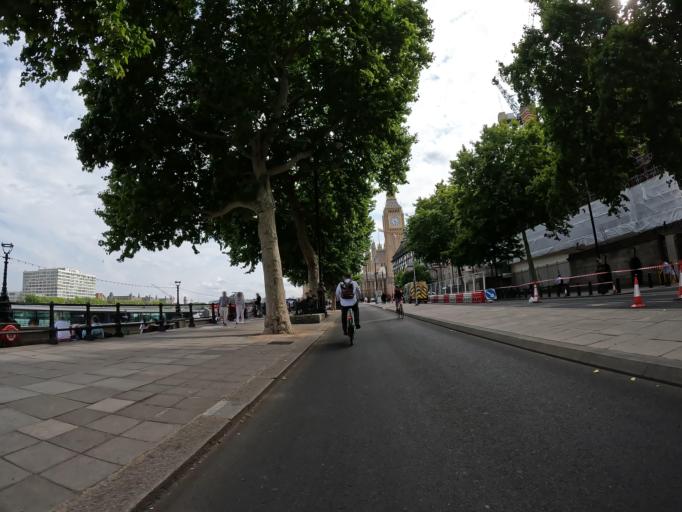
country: GB
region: England
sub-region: Greater London
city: Bromley
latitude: 51.3831
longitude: 0.0437
